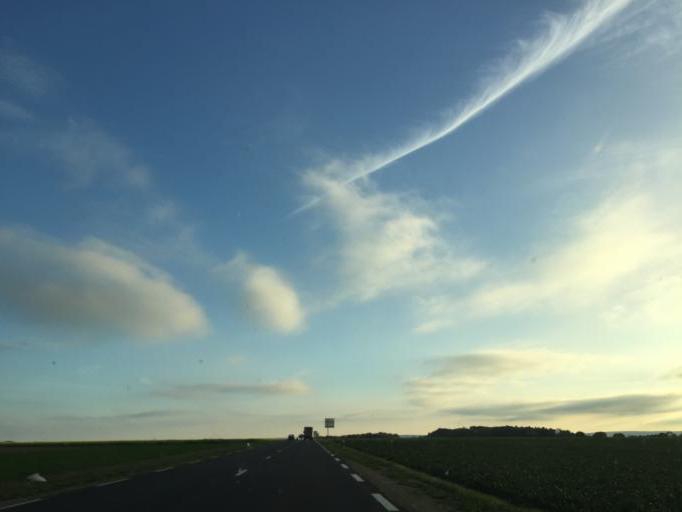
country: FR
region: Bourgogne
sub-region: Departement de l'Yonne
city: Sergines
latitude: 48.3509
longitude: 3.2318
